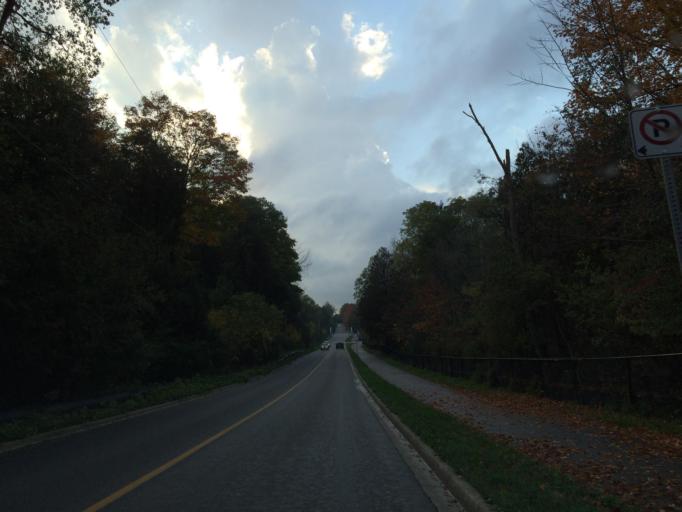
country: CA
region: Ontario
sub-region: Wellington County
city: Guelph
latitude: 43.5030
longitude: -80.2501
